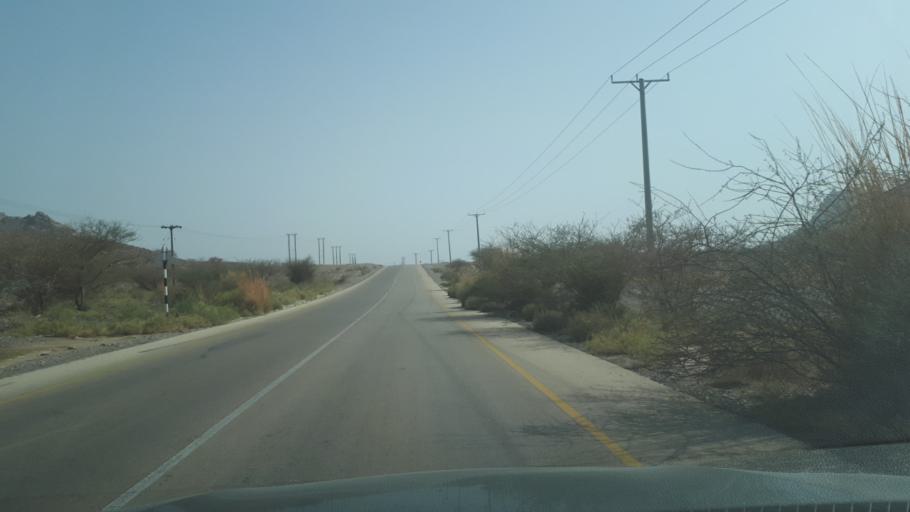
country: OM
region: Az Zahirah
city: `Ibri
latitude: 23.1886
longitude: 56.9237
